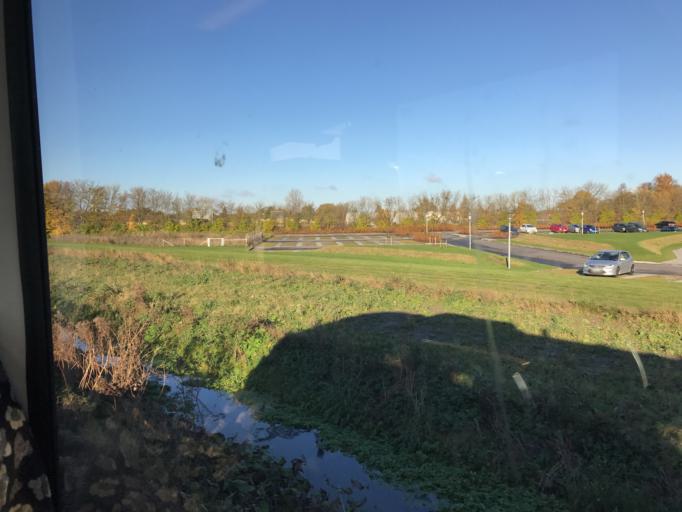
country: DK
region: Zealand
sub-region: Stevns Kommune
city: Store Heddinge
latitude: 55.3122
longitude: 12.3852
